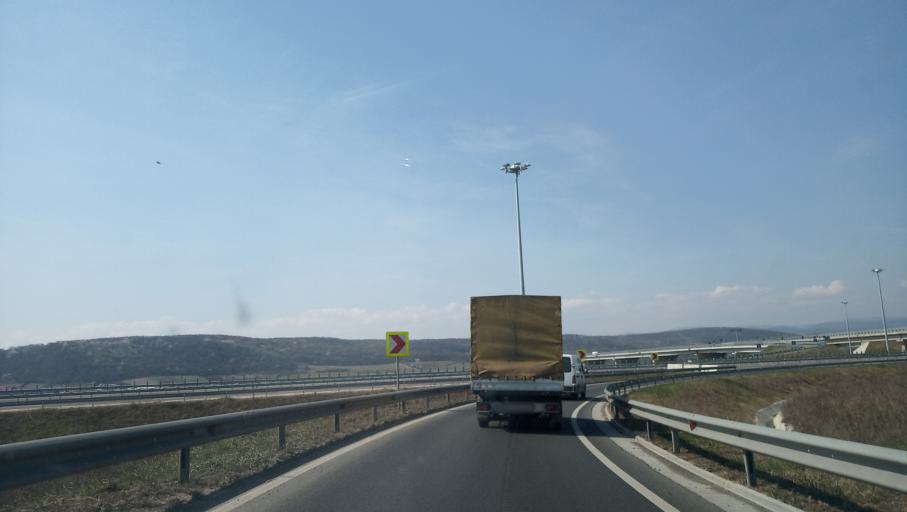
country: RO
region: Alba
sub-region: Municipiul Aiud
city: Aiud
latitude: 46.3274
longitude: 23.7309
